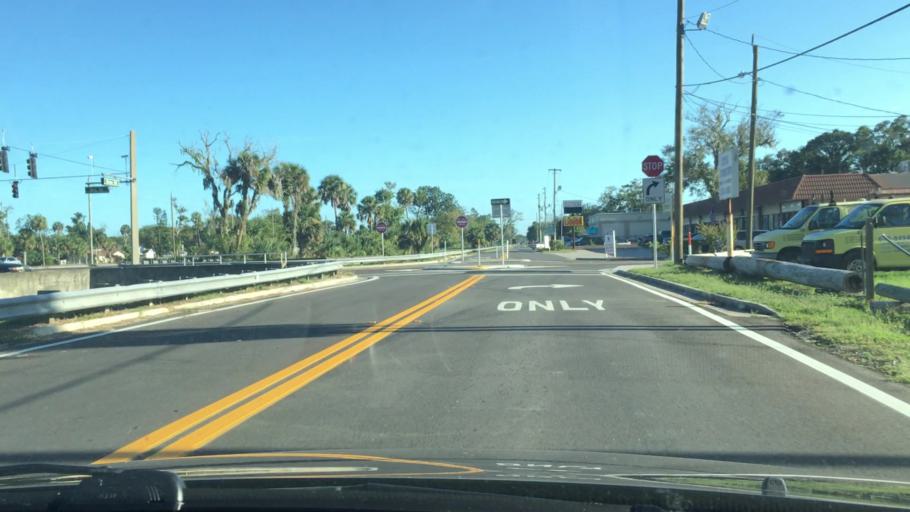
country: US
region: Florida
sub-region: Volusia County
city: Holly Hill
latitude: 29.2328
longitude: -81.0546
